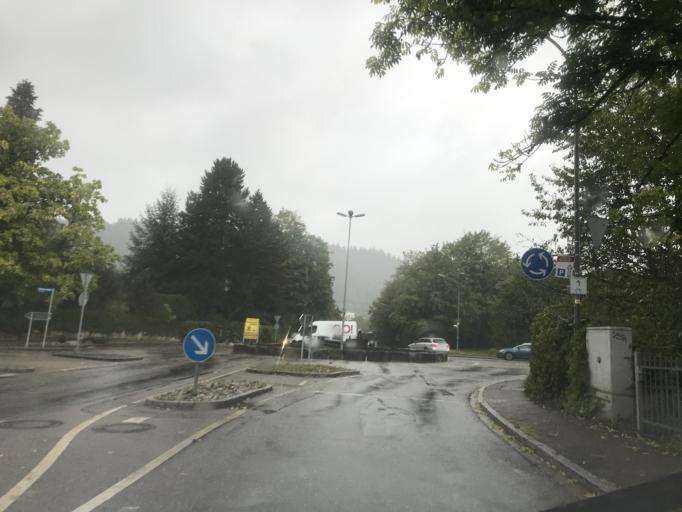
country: DE
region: Baden-Wuerttemberg
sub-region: Freiburg Region
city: Schopfheim
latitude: 47.6452
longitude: 7.8164
